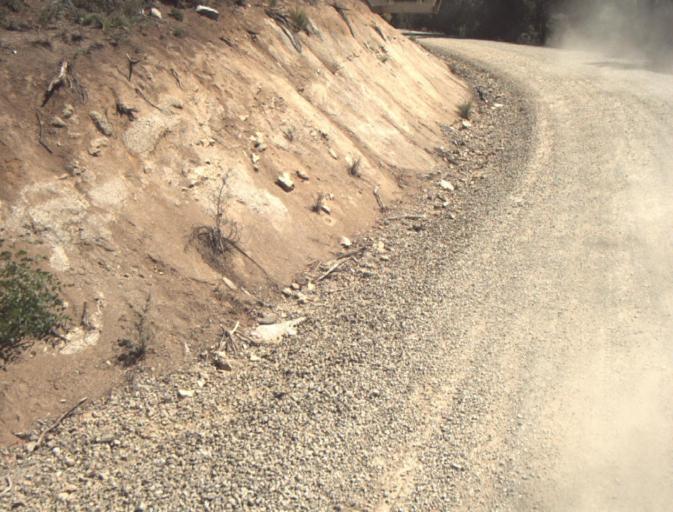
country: AU
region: Tasmania
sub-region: Dorset
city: Scottsdale
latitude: -41.3173
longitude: 147.4645
